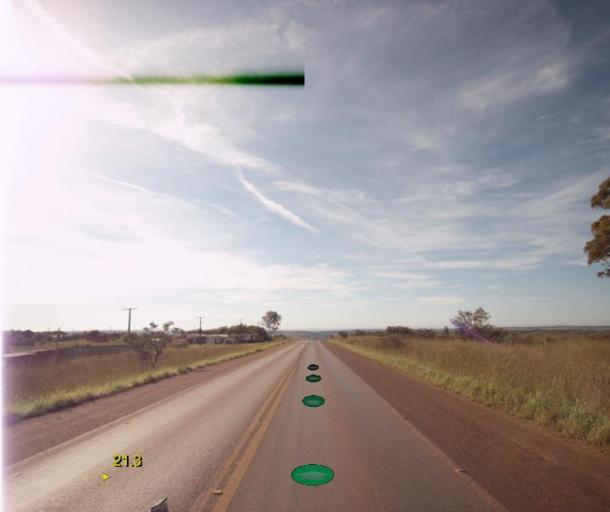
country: BR
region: Federal District
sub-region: Brasilia
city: Brasilia
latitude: -15.7392
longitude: -48.3866
